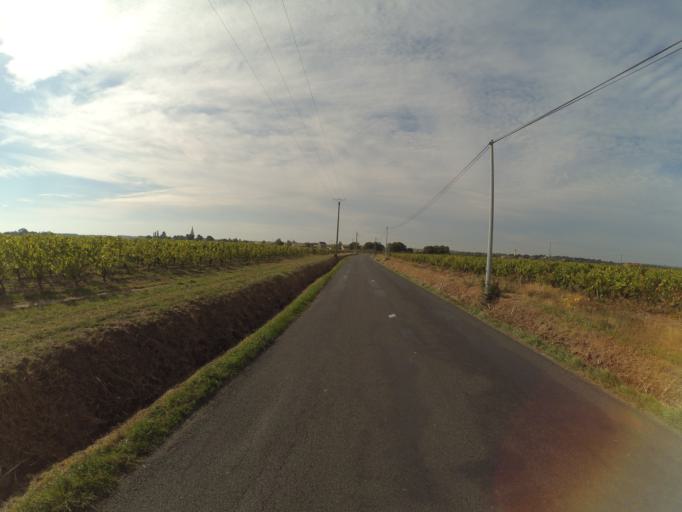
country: FR
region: Pays de la Loire
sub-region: Departement de Maine-et-Loire
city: Tillieres
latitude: 47.1509
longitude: -1.1643
